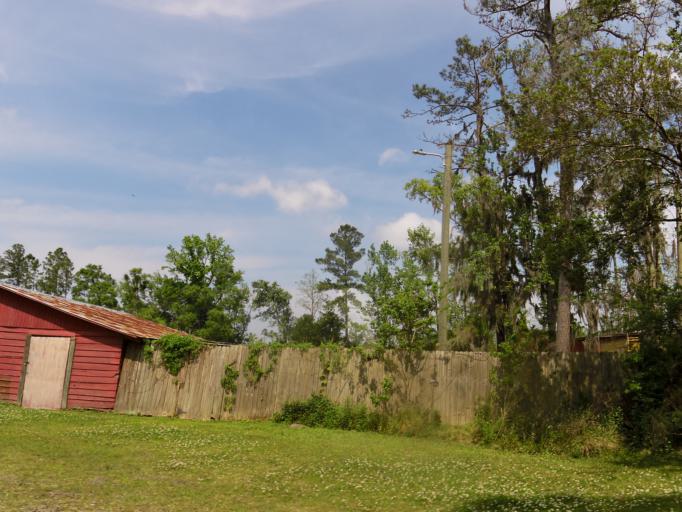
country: US
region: Georgia
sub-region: Camden County
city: Kingsland
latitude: 30.7910
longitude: -81.7165
